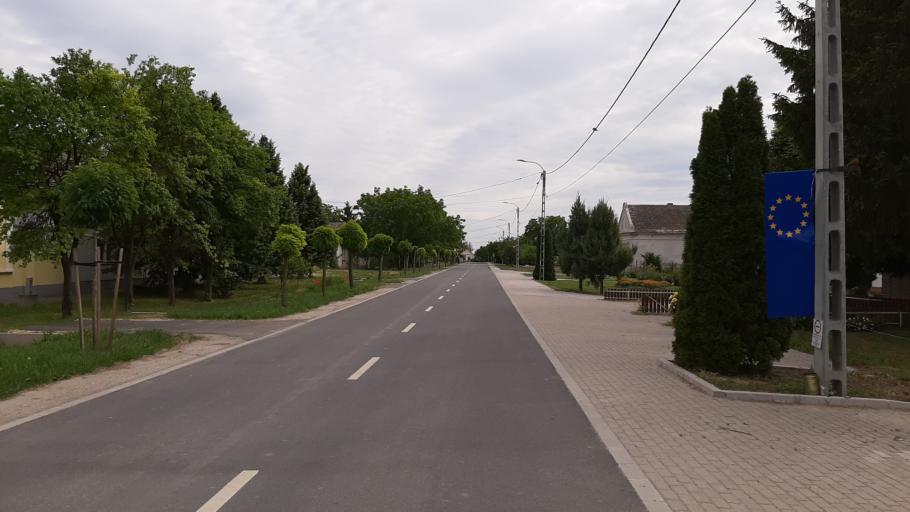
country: RO
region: Timis
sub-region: Comuna Beba Veche
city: Beba Veche
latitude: 46.1468
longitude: 20.2752
